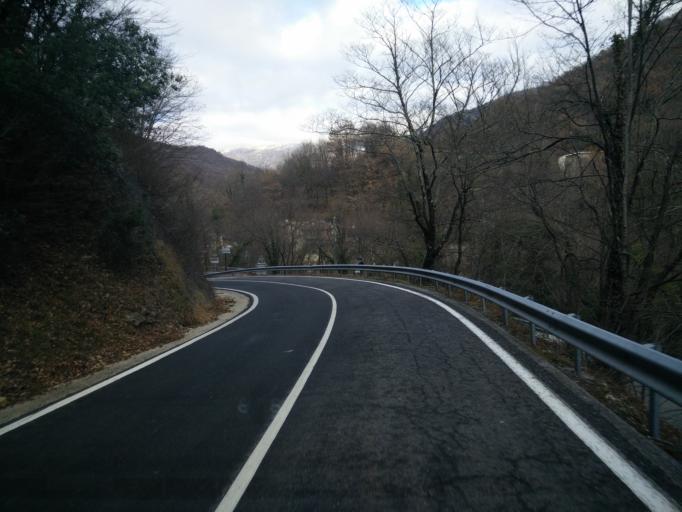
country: FR
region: Provence-Alpes-Cote d'Azur
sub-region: Departement des Alpes-Maritimes
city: Tourrettes-sur-Loup
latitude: 43.7603
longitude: 6.9898
